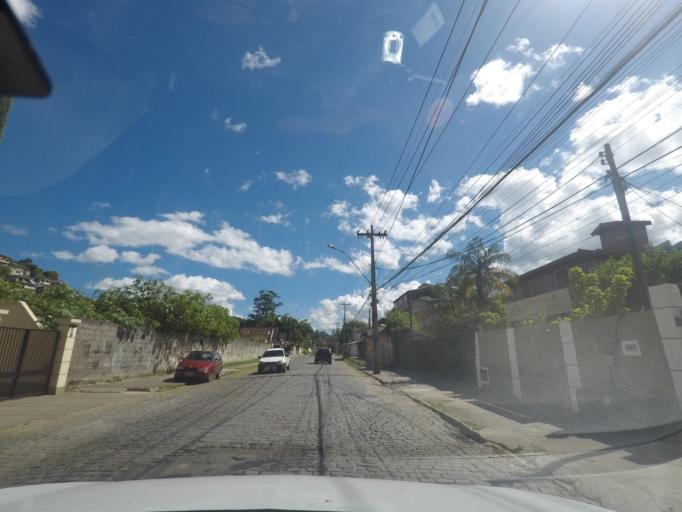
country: BR
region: Rio de Janeiro
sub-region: Teresopolis
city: Teresopolis
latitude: -22.4379
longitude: -42.9770
